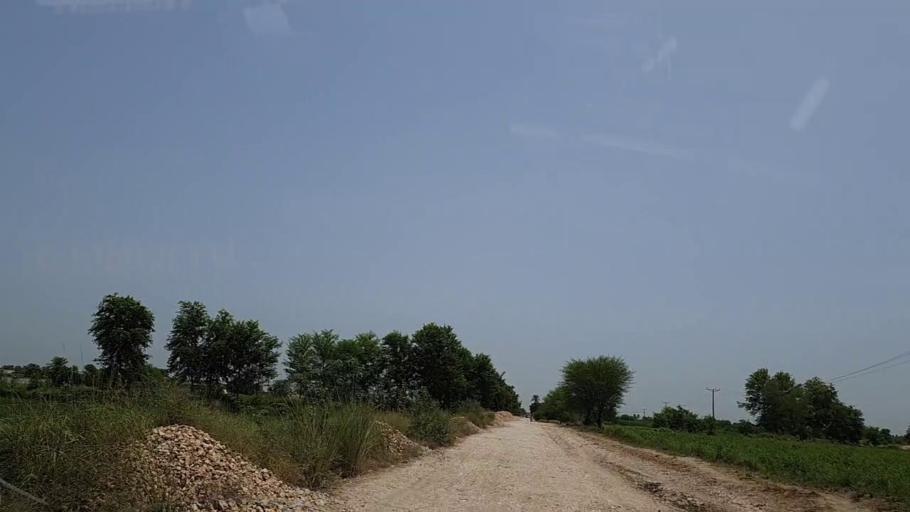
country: PK
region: Sindh
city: Tharu Shah
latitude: 26.9550
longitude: 68.0802
